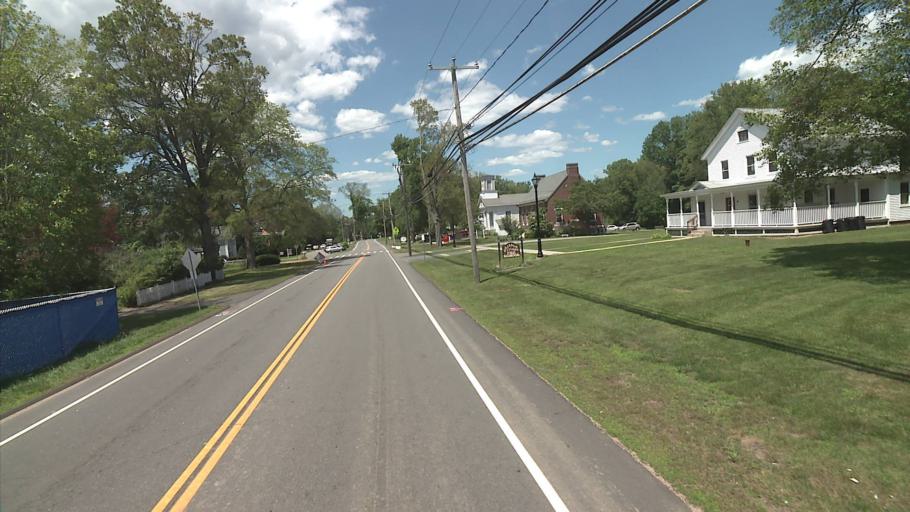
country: US
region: Connecticut
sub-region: Middlesex County
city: Moodus
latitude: 41.4997
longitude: -72.4496
